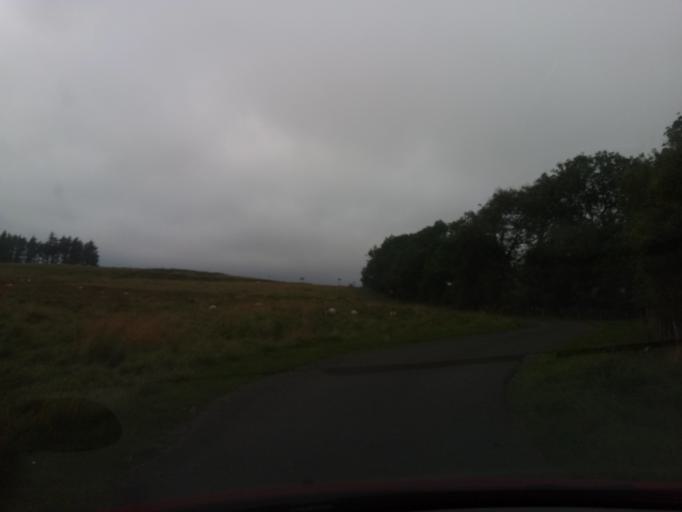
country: GB
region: England
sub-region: Northumberland
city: Otterburn
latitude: 55.2782
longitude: -2.0954
